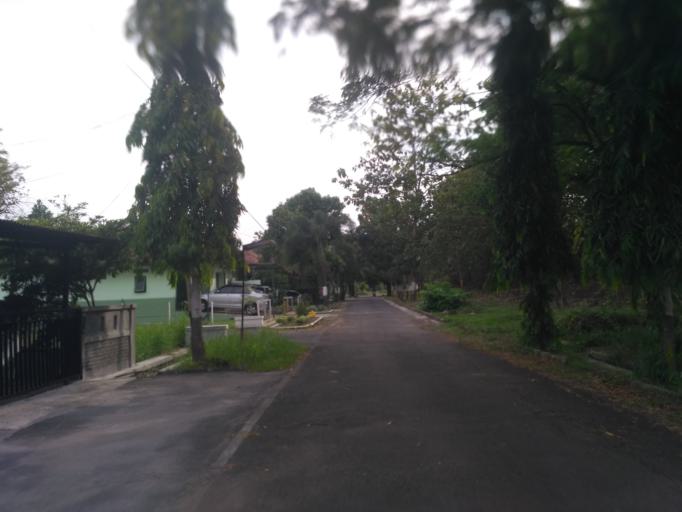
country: ID
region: Central Java
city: Semarang
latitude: -6.9890
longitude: 110.3748
